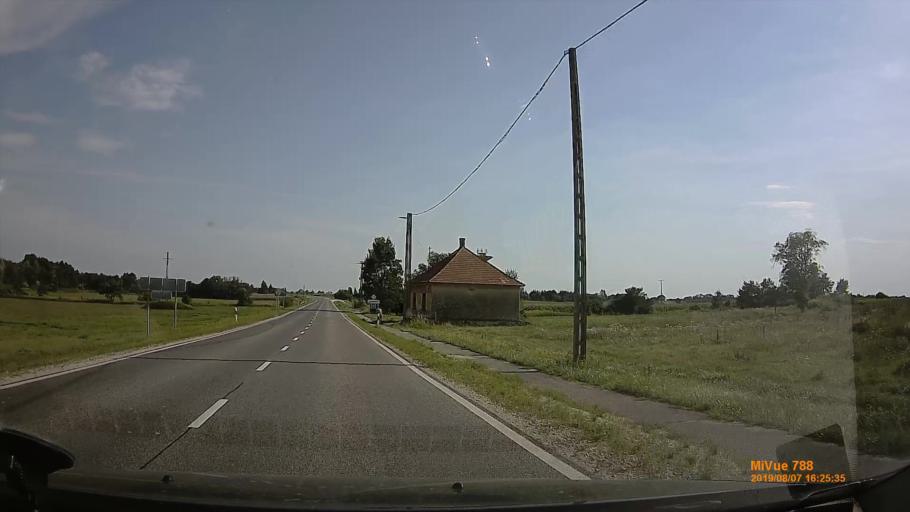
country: HU
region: Zala
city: Lenti
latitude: 46.7209
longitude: 16.5497
